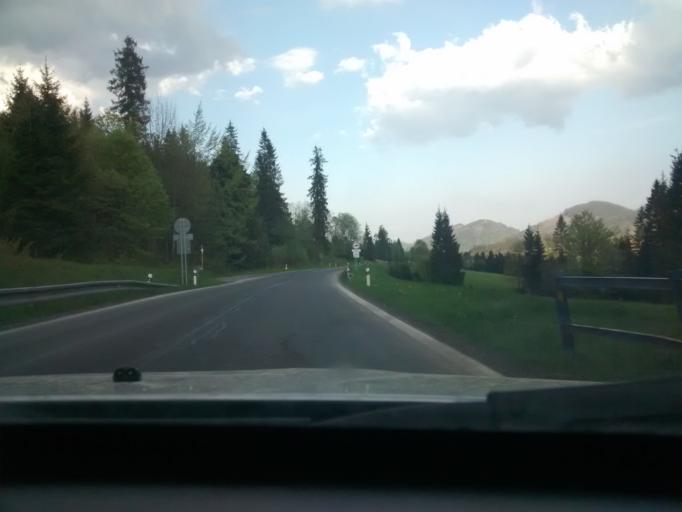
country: SK
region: Presovsky
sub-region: Okres Poprad
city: Zdiar
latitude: 49.2804
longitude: 20.2092
